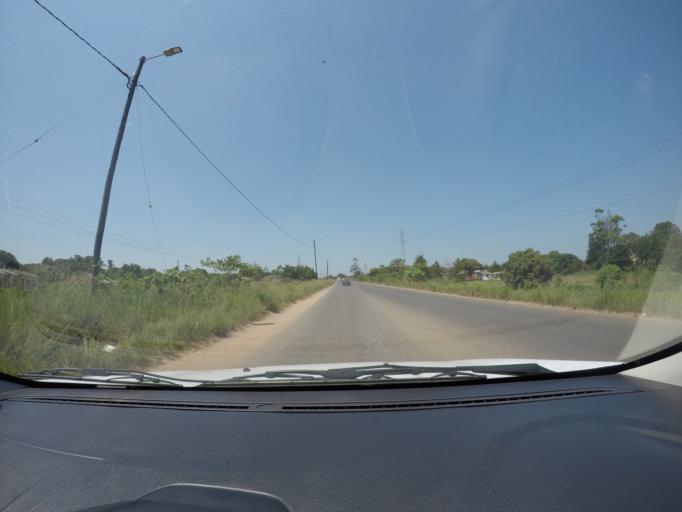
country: ZA
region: KwaZulu-Natal
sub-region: uThungulu District Municipality
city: eSikhawini
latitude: -28.8477
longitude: 31.9296
